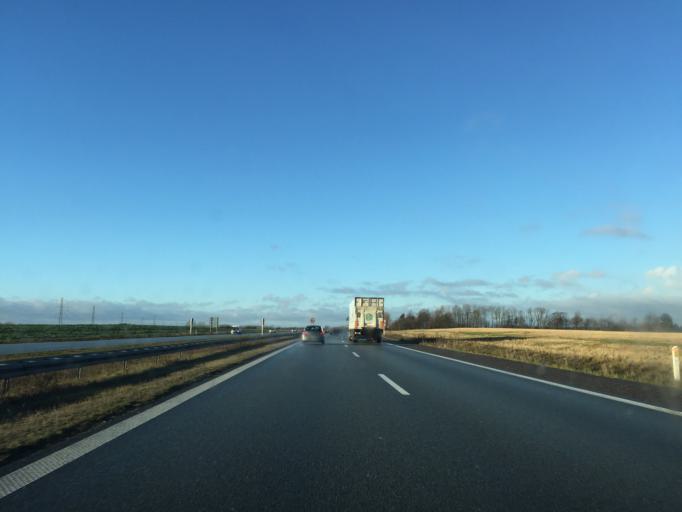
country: DK
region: Zealand
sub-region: Ringsted Kommune
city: Ringsted
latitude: 55.4537
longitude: 11.8524
